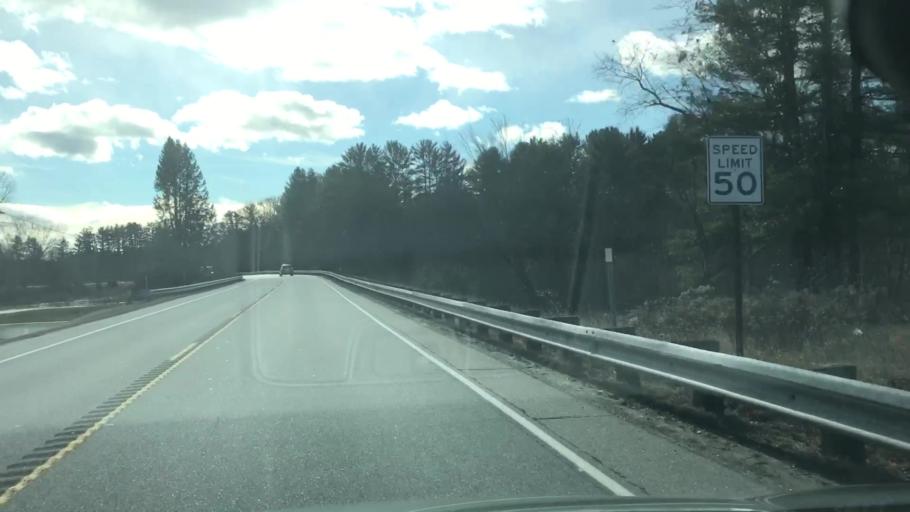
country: US
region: New Hampshire
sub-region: Merrimack County
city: Chichester
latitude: 43.2537
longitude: -71.3737
